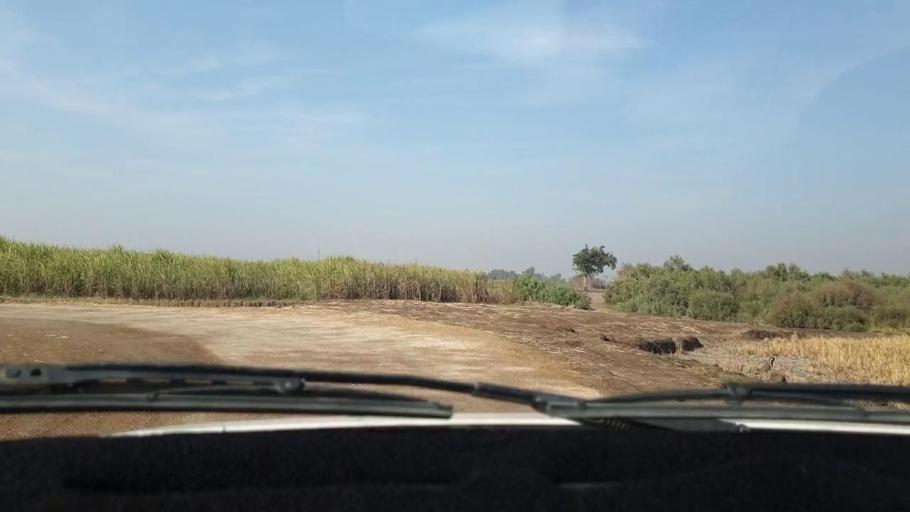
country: PK
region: Sindh
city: Tando Muhammad Khan
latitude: 25.0067
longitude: 68.4738
